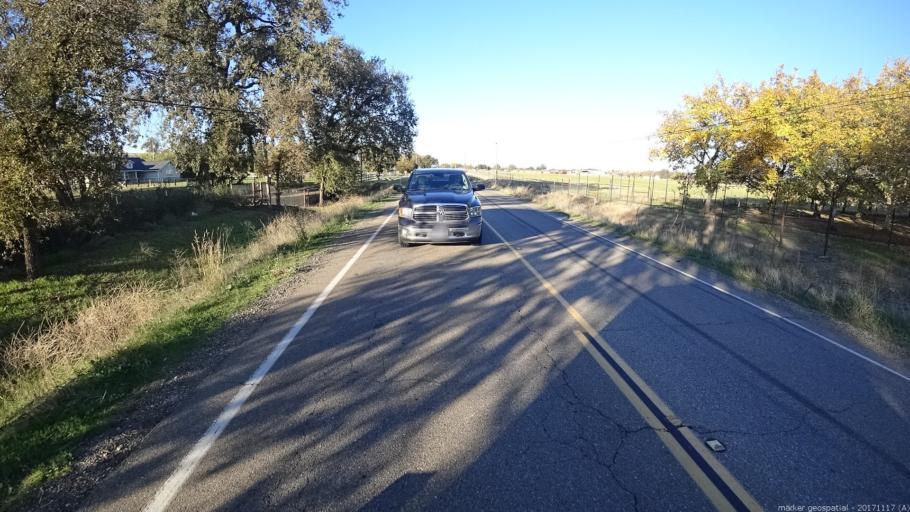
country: US
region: California
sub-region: Shasta County
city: Anderson
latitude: 40.4703
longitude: -122.2426
